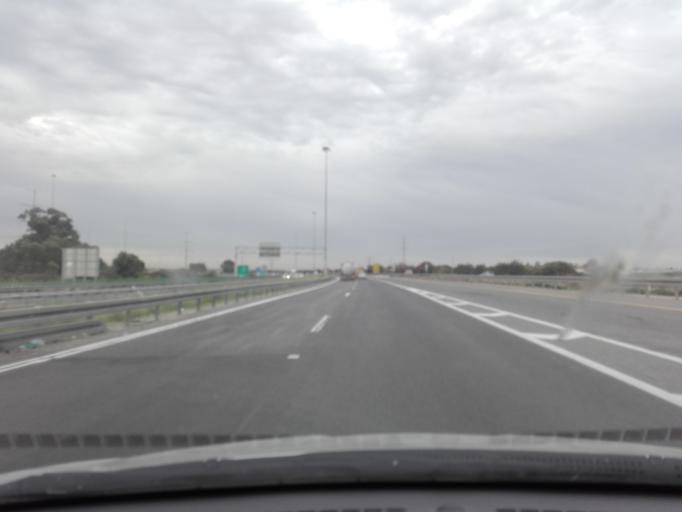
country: IL
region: Central District
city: Ramla
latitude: 31.9061
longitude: 34.8902
